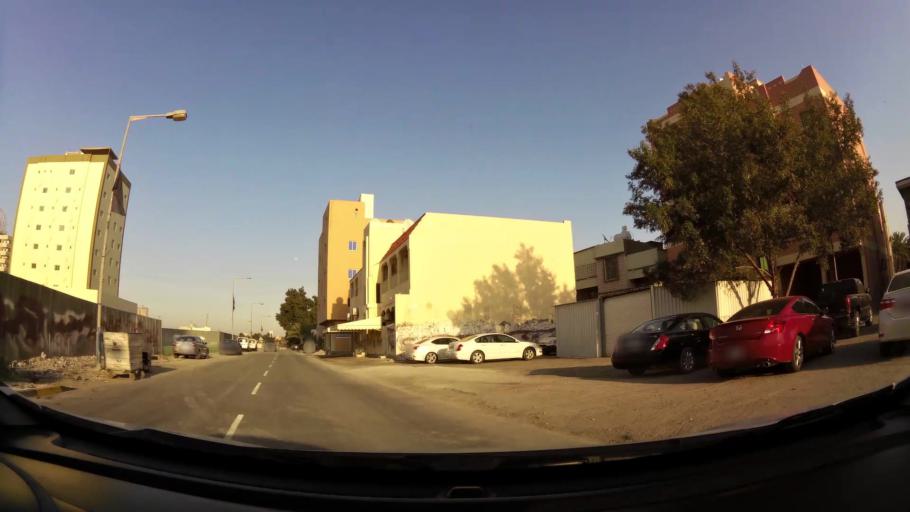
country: BH
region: Manama
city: Jidd Hafs
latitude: 26.2249
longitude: 50.5573
